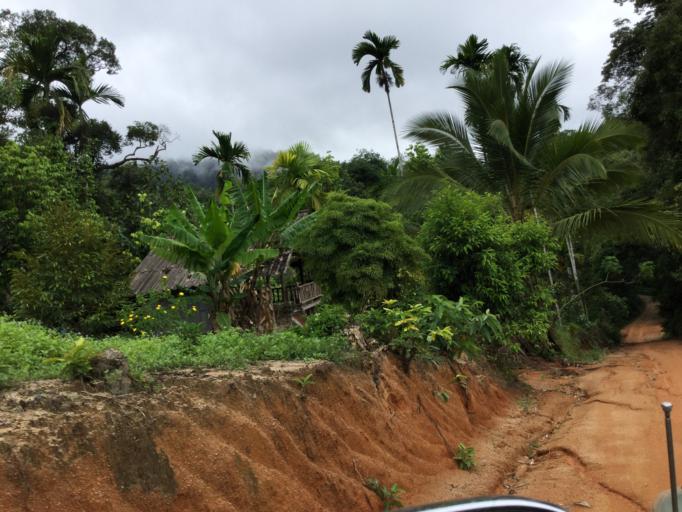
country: TH
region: Nakhon Si Thammarat
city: Ko Pha Ngan
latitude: 9.7335
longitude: 100.0509
